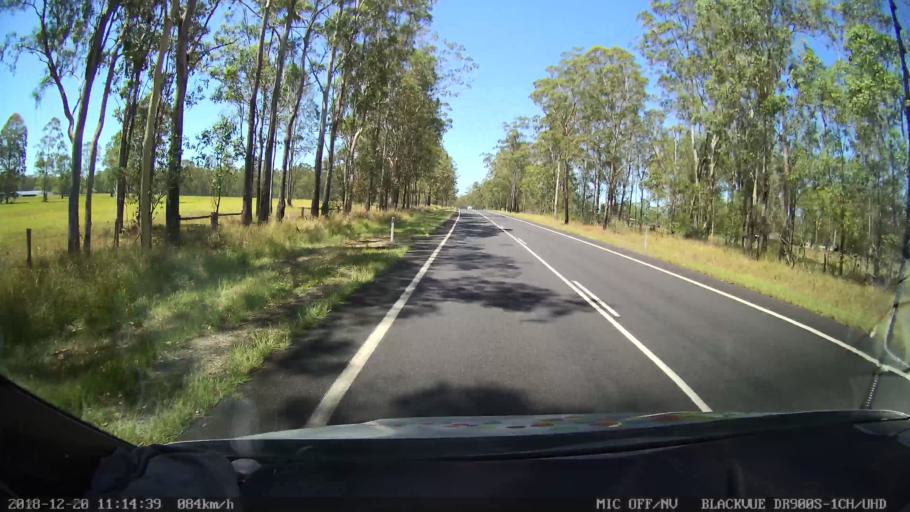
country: AU
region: New South Wales
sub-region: Richmond Valley
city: Casino
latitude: -29.0031
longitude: 153.0077
